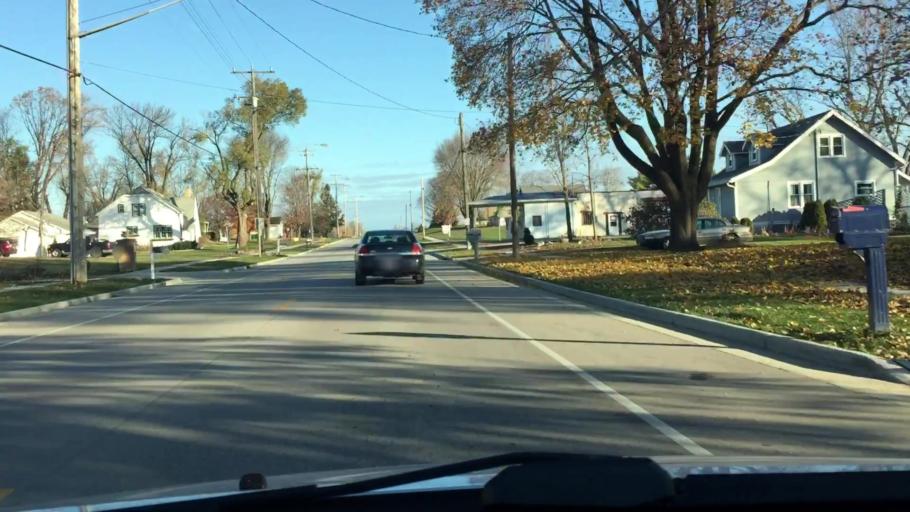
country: US
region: Wisconsin
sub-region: Dodge County
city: Lomira
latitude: 43.5933
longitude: -88.4502
